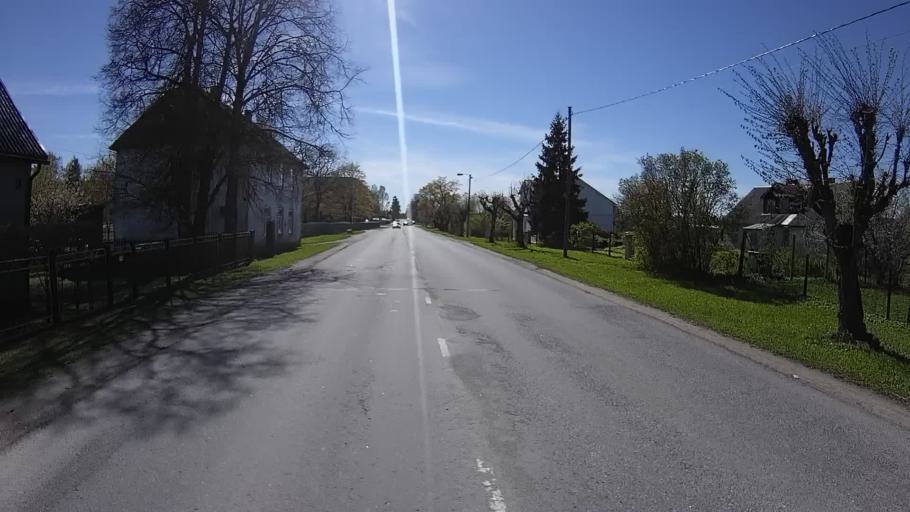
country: EE
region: Laeaene-Virumaa
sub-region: Tapa vald
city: Tapa
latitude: 59.2705
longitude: 25.9650
